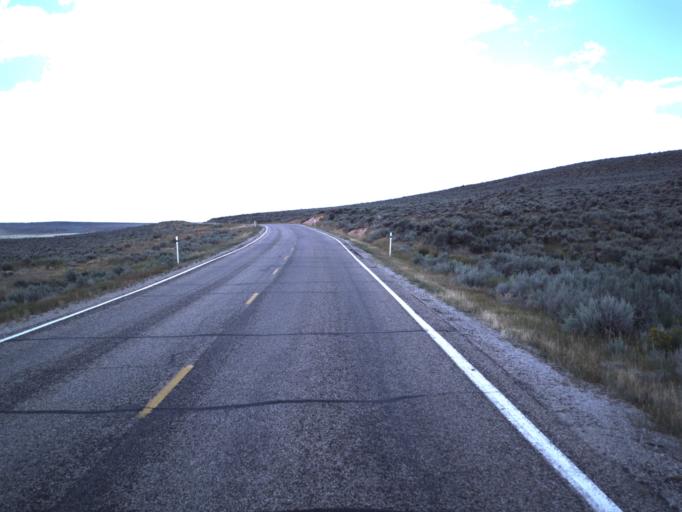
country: US
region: Utah
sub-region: Rich County
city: Randolph
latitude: 41.7933
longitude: -111.2222
